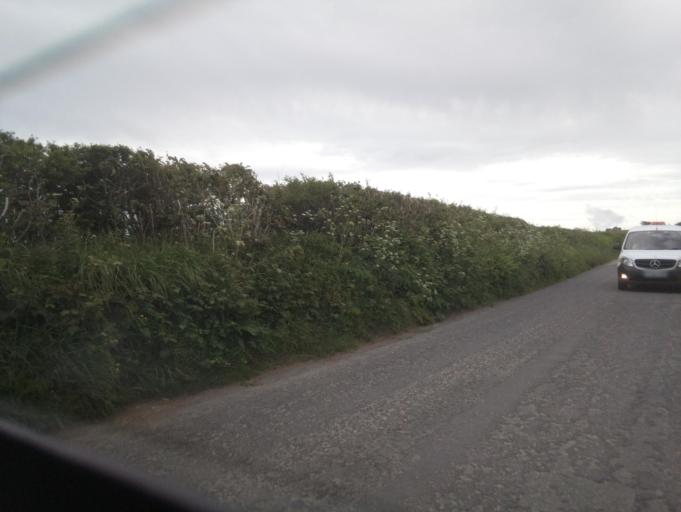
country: GB
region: England
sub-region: Devon
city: Dartmouth
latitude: 50.3228
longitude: -3.6380
